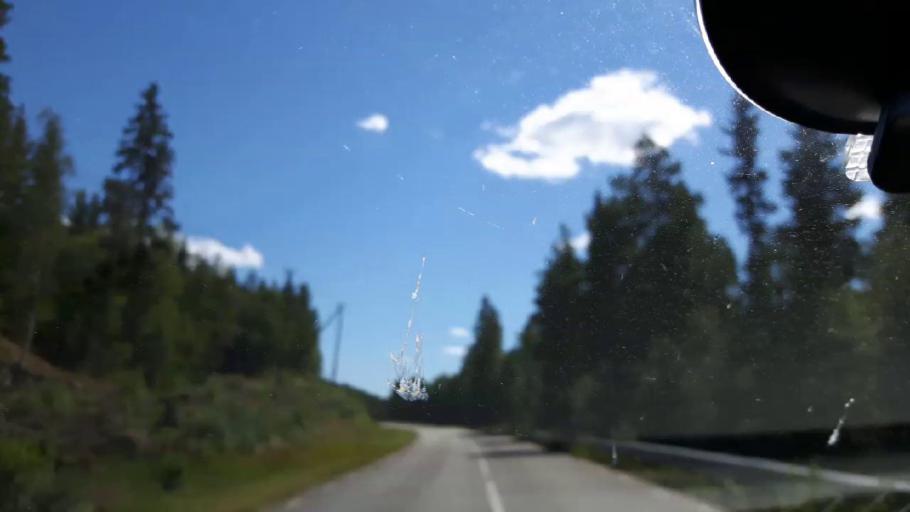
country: SE
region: Vaesternorrland
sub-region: Ange Kommun
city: Fransta
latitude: 62.7318
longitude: 16.3289
